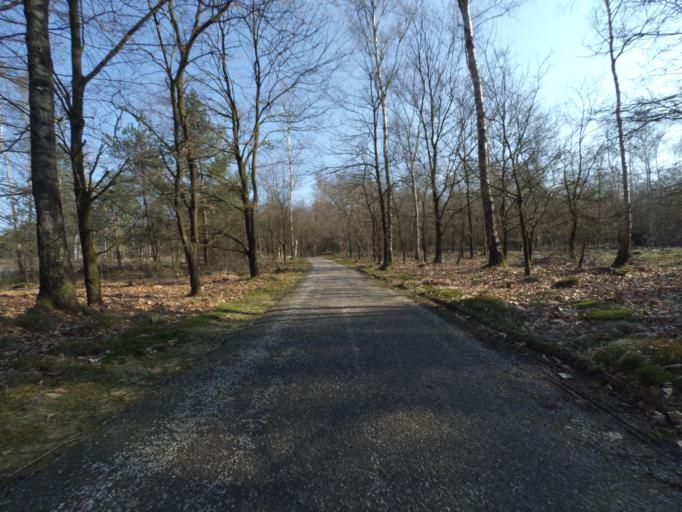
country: NL
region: Gelderland
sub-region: Gemeente Arnhem
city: Hoogkamp
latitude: 52.0444
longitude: 5.8523
